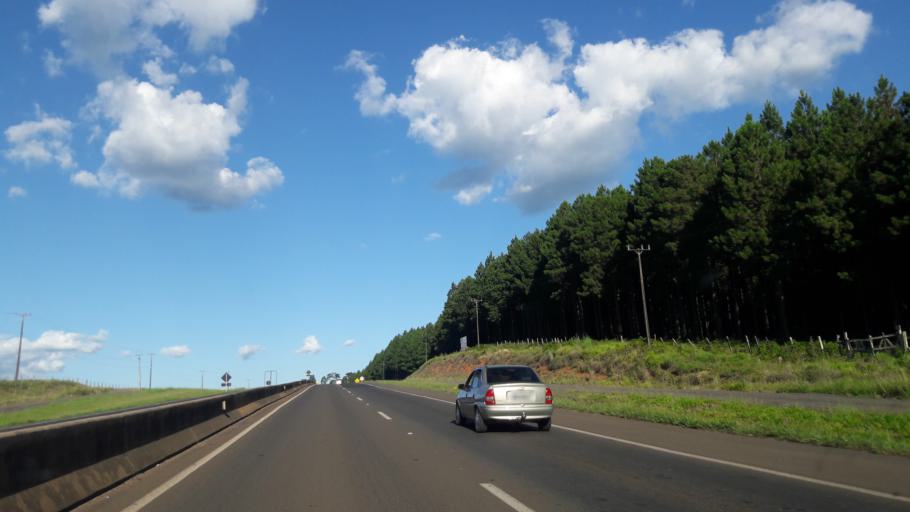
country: BR
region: Parana
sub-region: Guarapuava
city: Guarapuava
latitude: -25.3440
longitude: -51.4394
